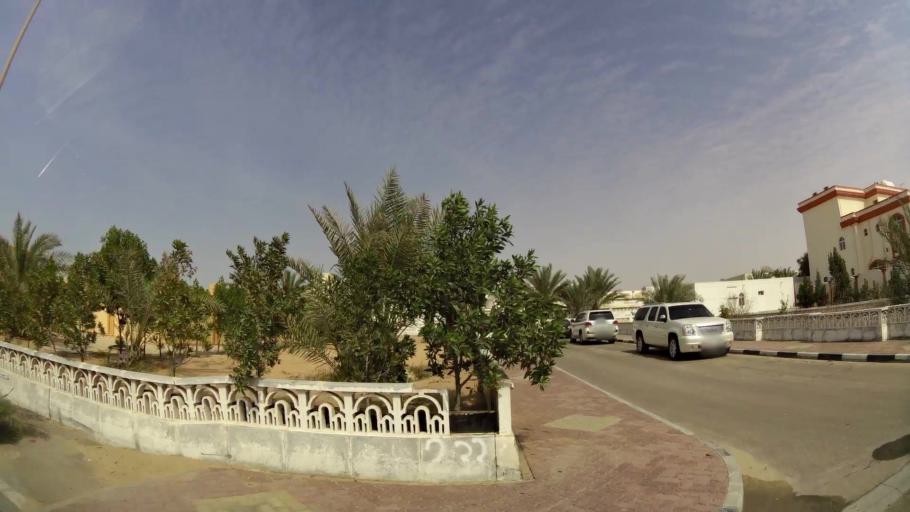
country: AE
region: Abu Dhabi
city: Abu Dhabi
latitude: 24.5433
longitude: 54.6633
